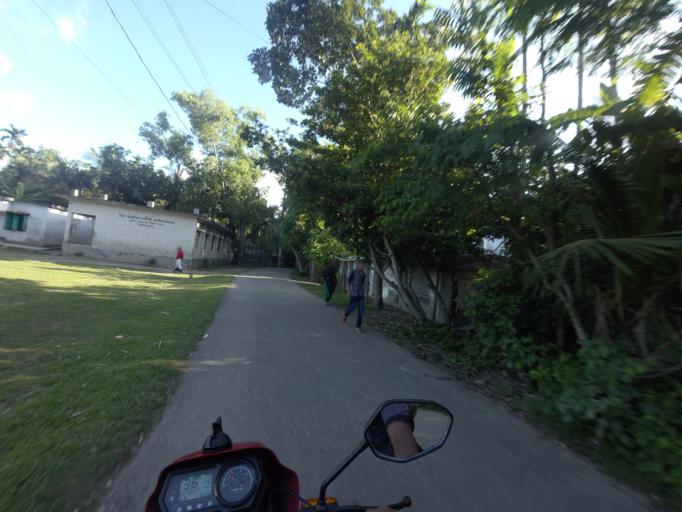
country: BD
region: Khulna
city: Bhatpara Abhaynagar
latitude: 22.9229
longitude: 89.5179
